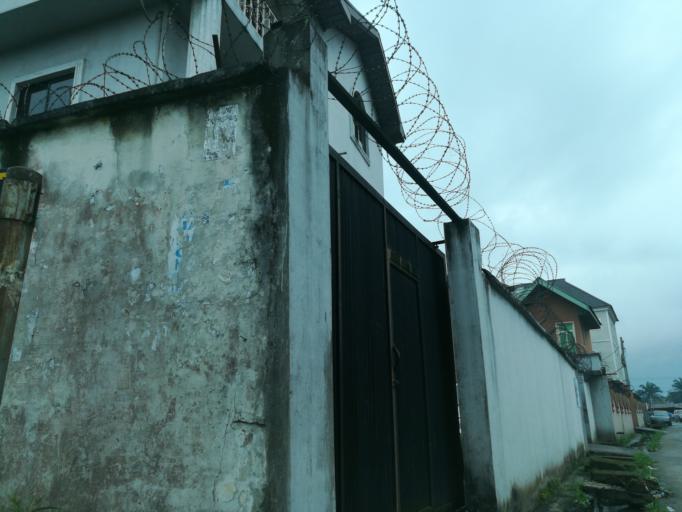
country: NG
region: Rivers
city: Port Harcourt
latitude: 4.8139
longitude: 7.0180
